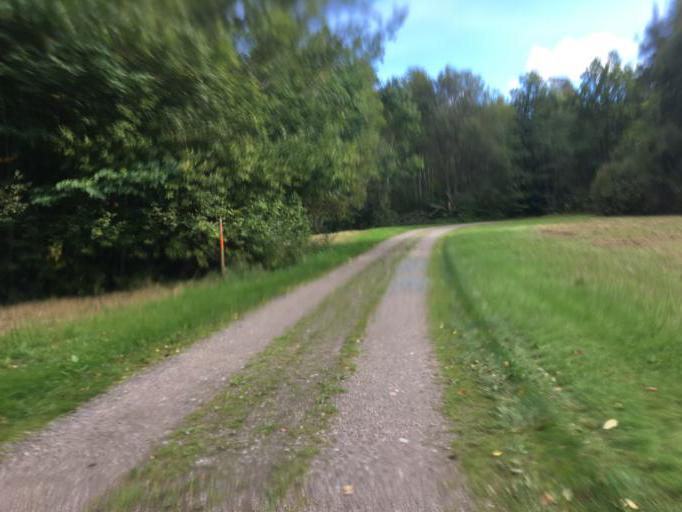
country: SE
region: Soedermanland
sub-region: Eskilstuna Kommun
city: Eskilstuna
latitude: 59.4585
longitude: 16.6566
